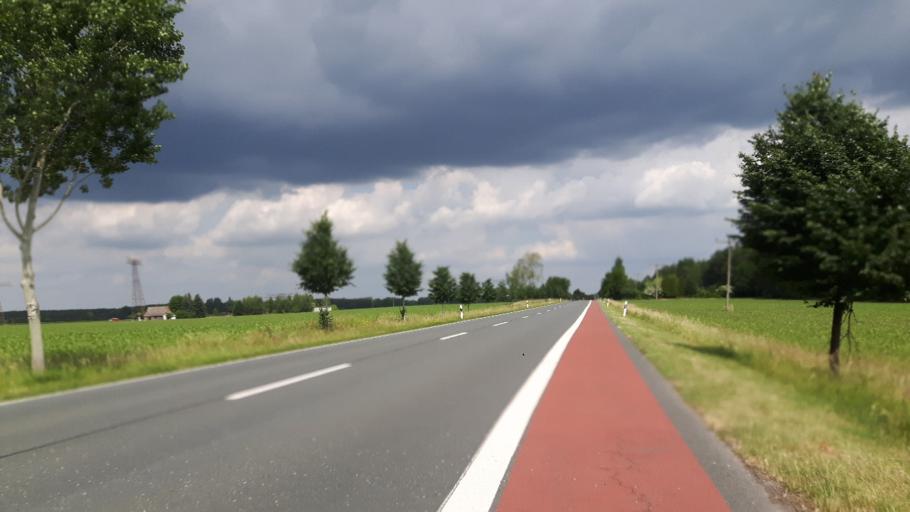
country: DE
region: Saxony-Anhalt
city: Schlaitz
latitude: 51.6815
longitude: 12.4465
